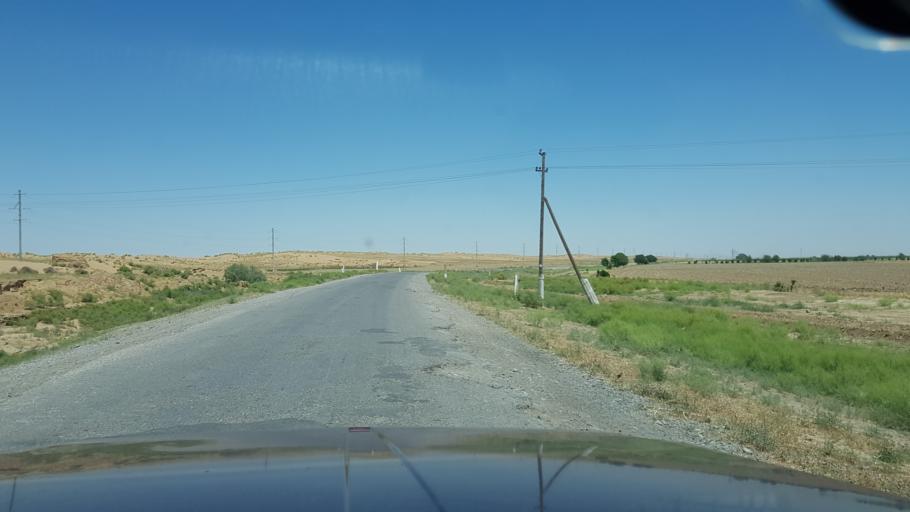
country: TM
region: Ahal
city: Annau
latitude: 37.8568
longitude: 58.7074
